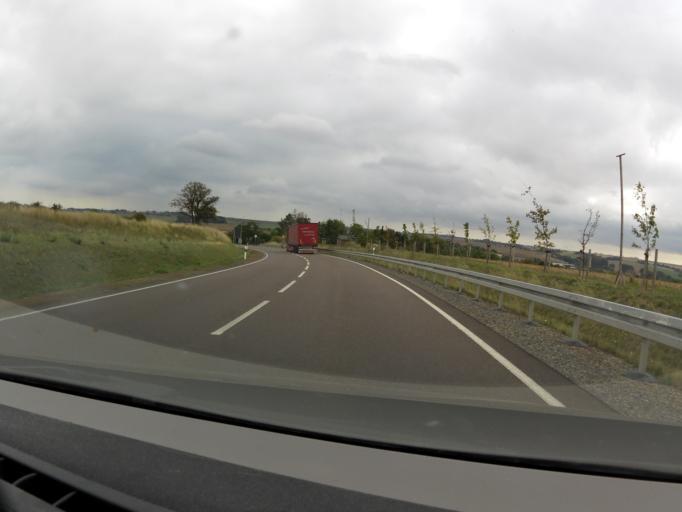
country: DE
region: Saxony-Anhalt
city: Sandersleben
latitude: 51.6814
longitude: 11.5751
